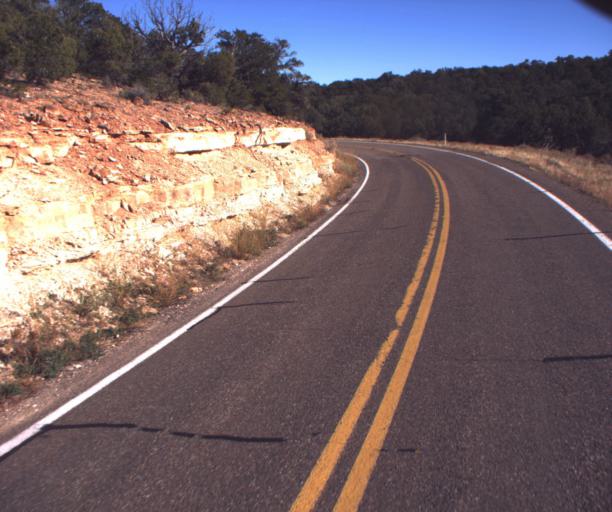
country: US
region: Arizona
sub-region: Coconino County
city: Fredonia
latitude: 36.7398
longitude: -112.1070
